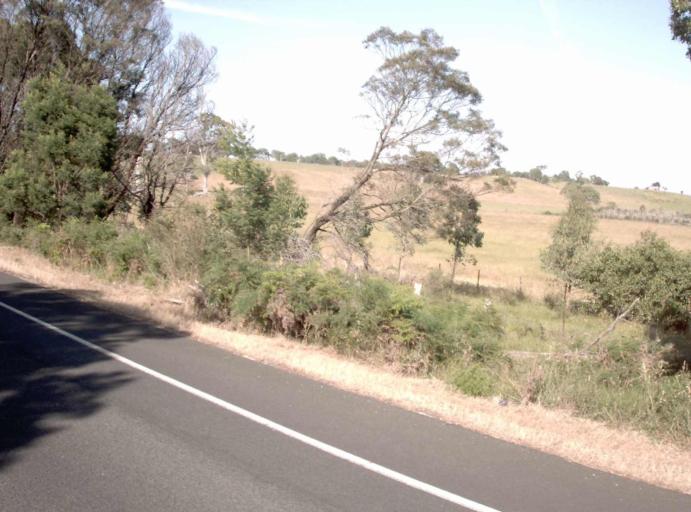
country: AU
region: Victoria
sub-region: East Gippsland
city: Lakes Entrance
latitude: -37.8495
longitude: 147.8482
